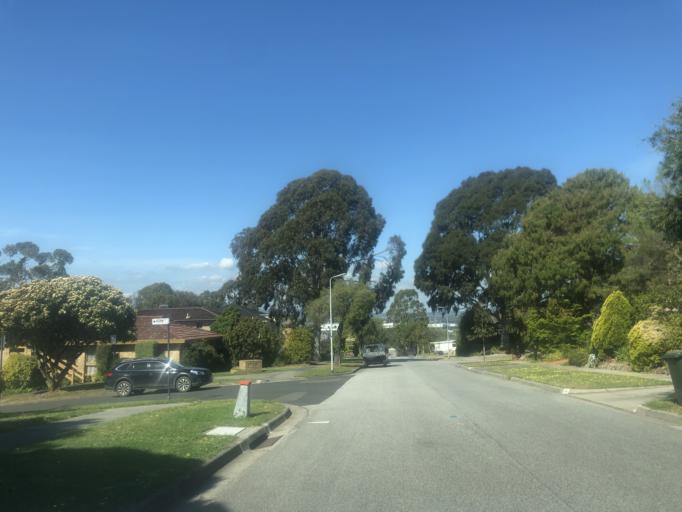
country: AU
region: Victoria
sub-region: Monash
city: Mulgrave
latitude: -37.9058
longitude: 145.1919
